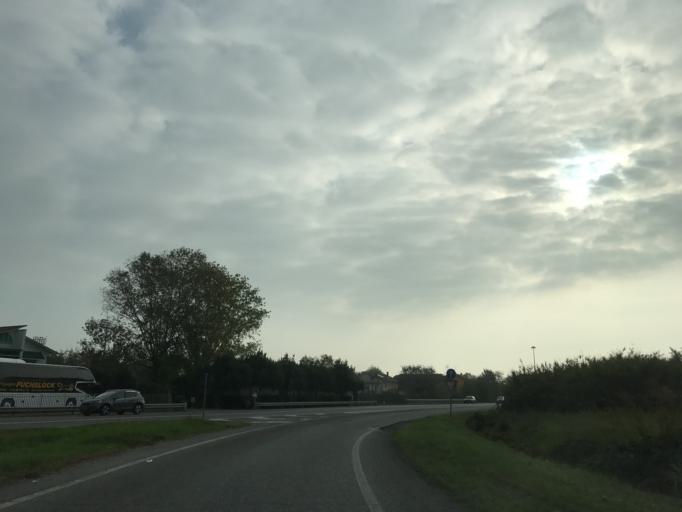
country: IT
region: Emilia-Romagna
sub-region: Forli-Cesena
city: Cesenatico
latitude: 44.1912
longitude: 12.4005
